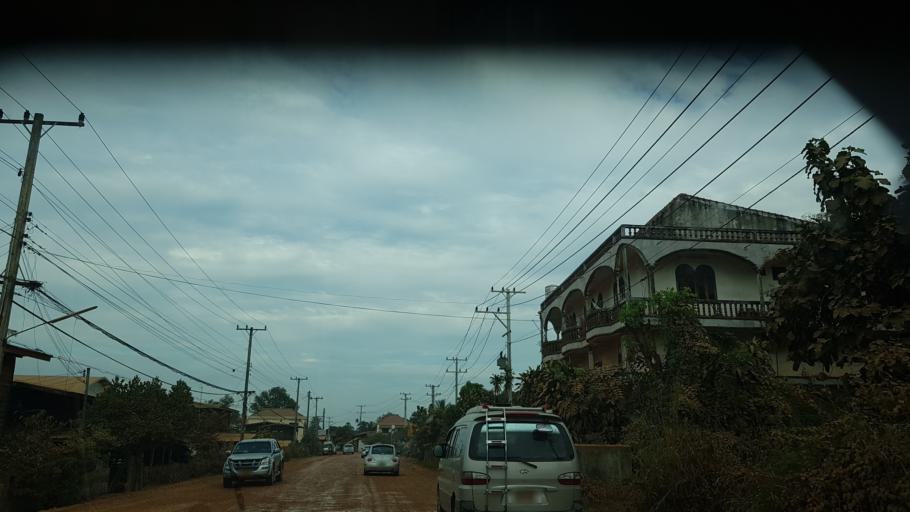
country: TH
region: Nong Khai
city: Nong Khai
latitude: 17.8929
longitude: 102.7476
